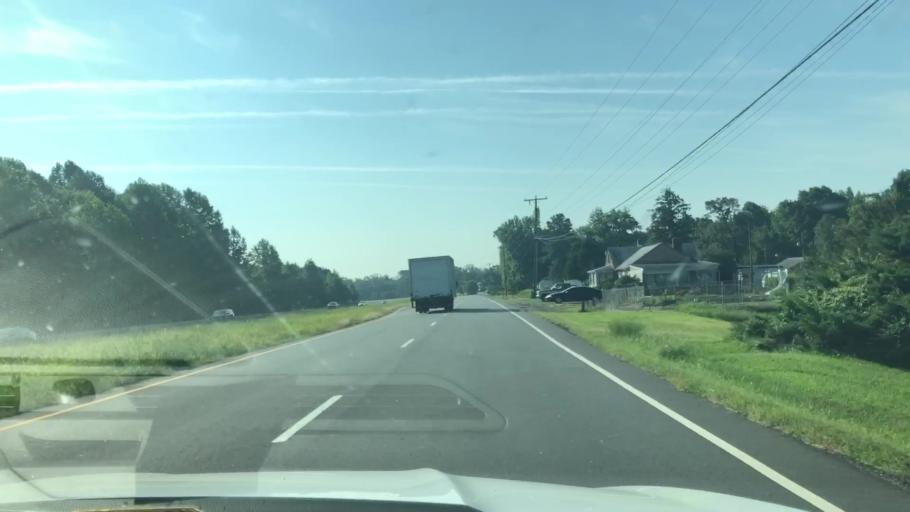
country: US
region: Virginia
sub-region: Richmond County
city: Warsaw
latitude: 37.9376
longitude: -76.7436
